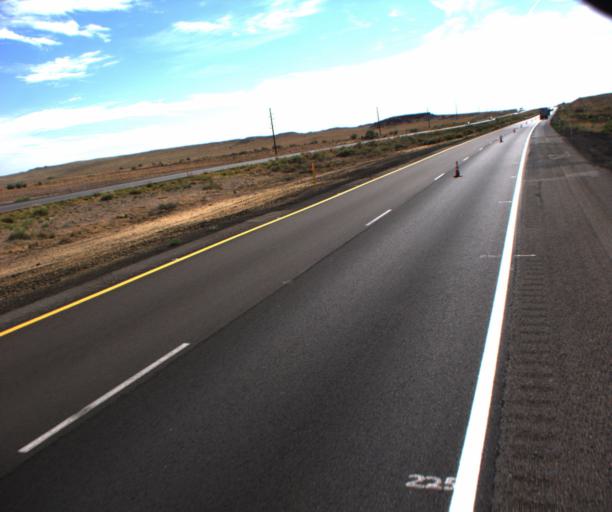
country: US
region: Arizona
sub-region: Navajo County
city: Holbrook
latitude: 34.9911
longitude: -109.9880
